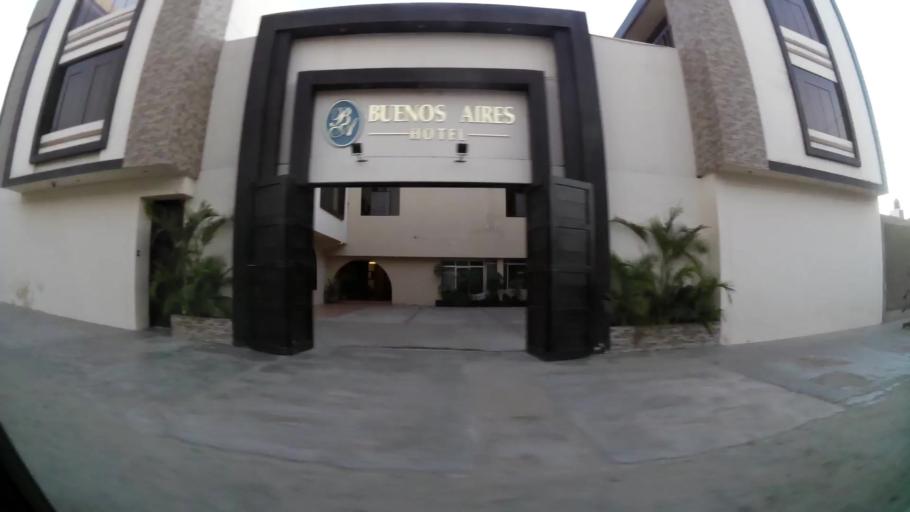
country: PE
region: Ancash
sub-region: Provincia de Santa
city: Buenos Aires
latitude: -9.1227
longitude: -78.5349
